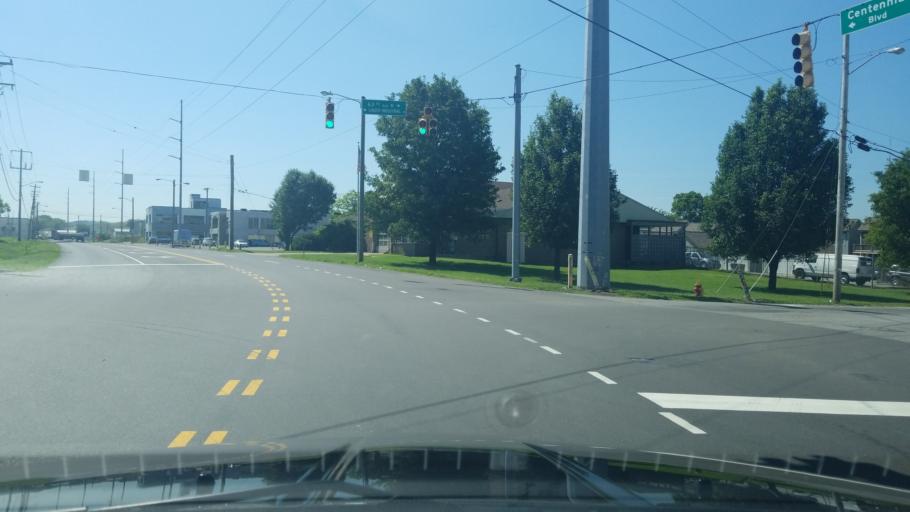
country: US
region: Tennessee
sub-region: Davidson County
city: Belle Meade
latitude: 36.1694
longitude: -86.8622
